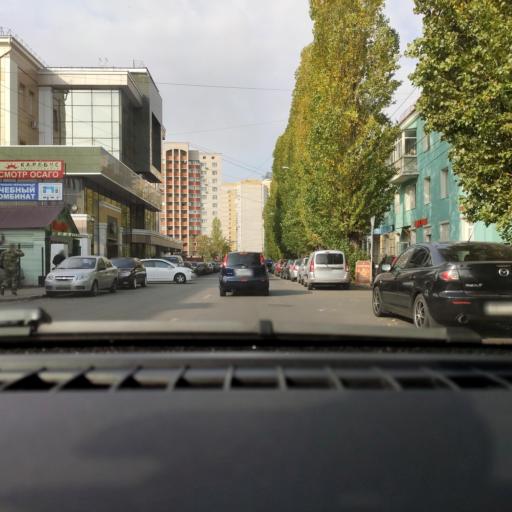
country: RU
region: Voronezj
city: Voronezh
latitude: 51.6802
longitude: 39.2577
